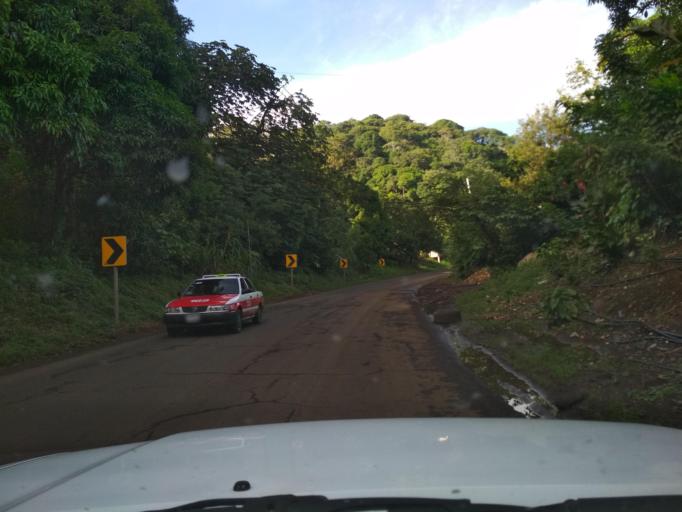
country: MX
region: Veracruz
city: Catemaco
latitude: 18.3894
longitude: -95.1239
